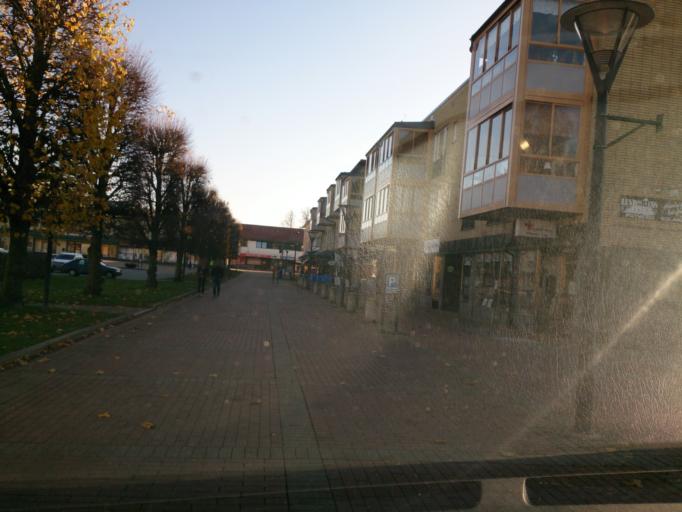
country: SE
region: OEstergoetland
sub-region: Atvidabergs Kommun
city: Atvidaberg
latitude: 58.2020
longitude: 15.9969
